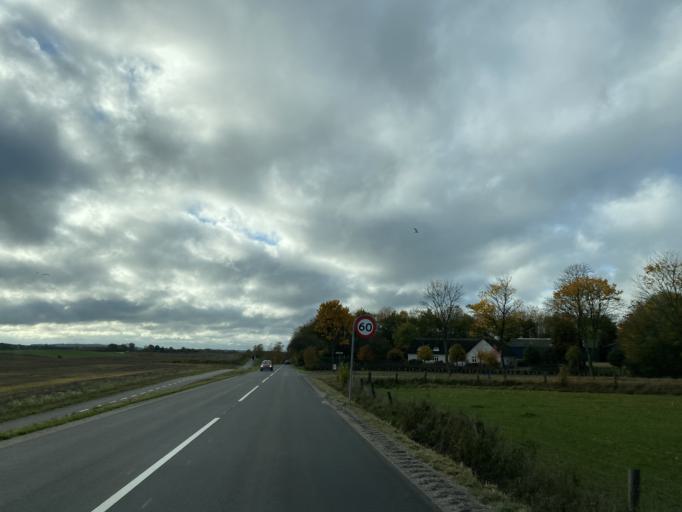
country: DK
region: Central Jutland
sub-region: Favrskov Kommune
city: Hammel
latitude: 56.2543
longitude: 9.8344
